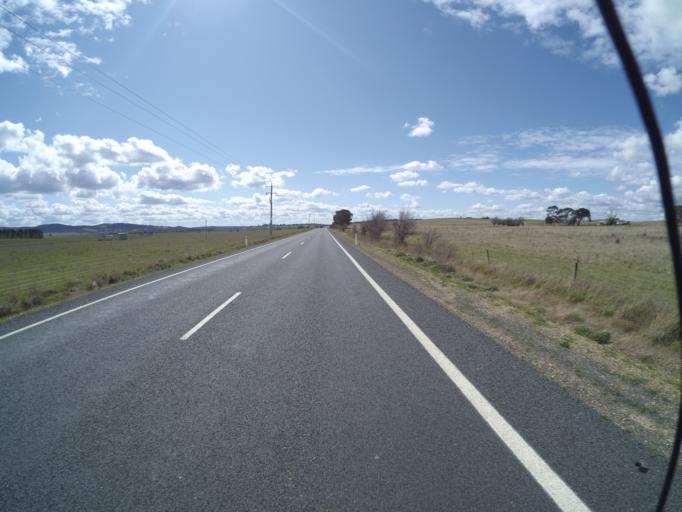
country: AU
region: New South Wales
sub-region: Goulburn Mulwaree
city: Goulburn
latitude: -34.8568
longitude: 149.6838
